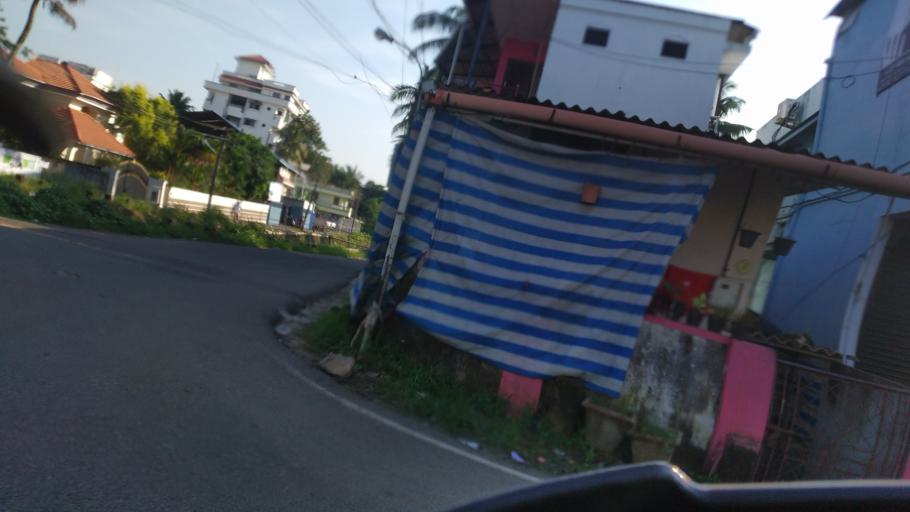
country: IN
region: Kerala
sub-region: Ernakulam
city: Cochin
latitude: 9.9851
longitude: 76.2914
